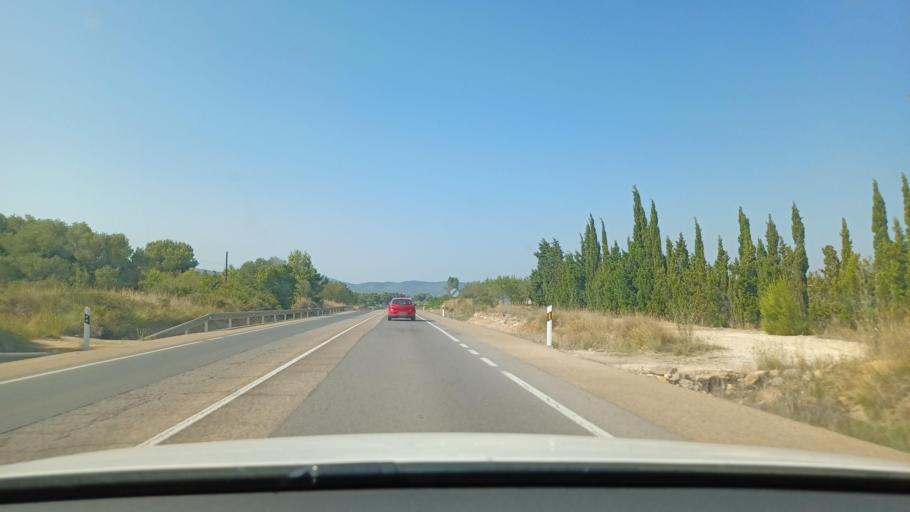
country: ES
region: Valencia
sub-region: Provincia de Castello
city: Alcala de Xivert
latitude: 40.2881
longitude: 0.2252
